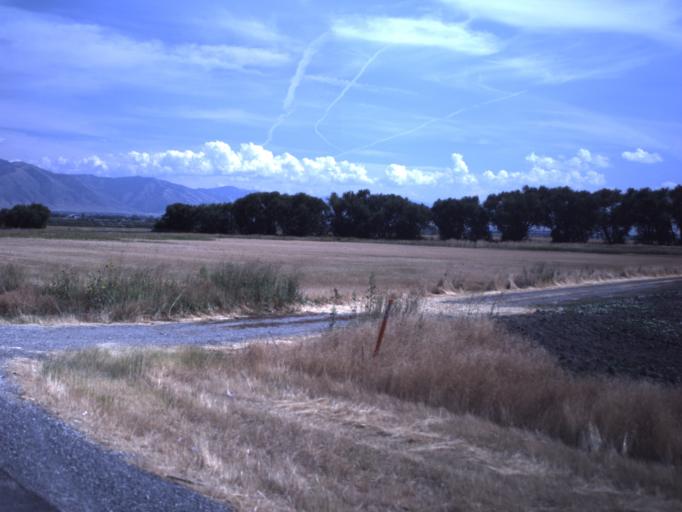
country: US
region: Utah
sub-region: Cache County
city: Mendon
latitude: 41.7485
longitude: -111.9699
